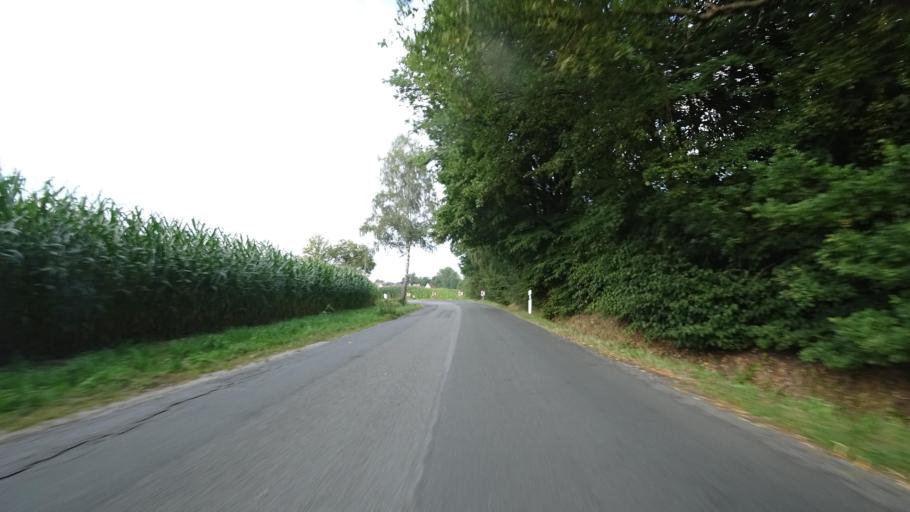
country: DE
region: North Rhine-Westphalia
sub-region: Regierungsbezirk Detmold
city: Steinhagen
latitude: 51.9587
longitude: 8.4679
